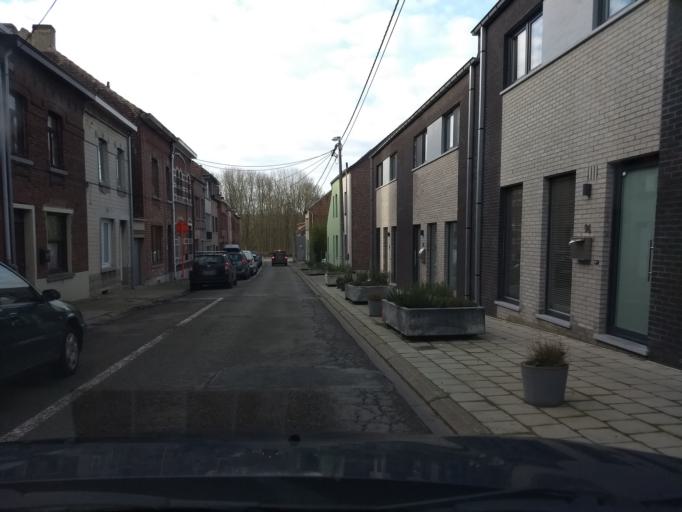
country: BE
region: Flanders
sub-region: Provincie Vlaams-Brabant
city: Halle
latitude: 50.7105
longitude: 4.2371
